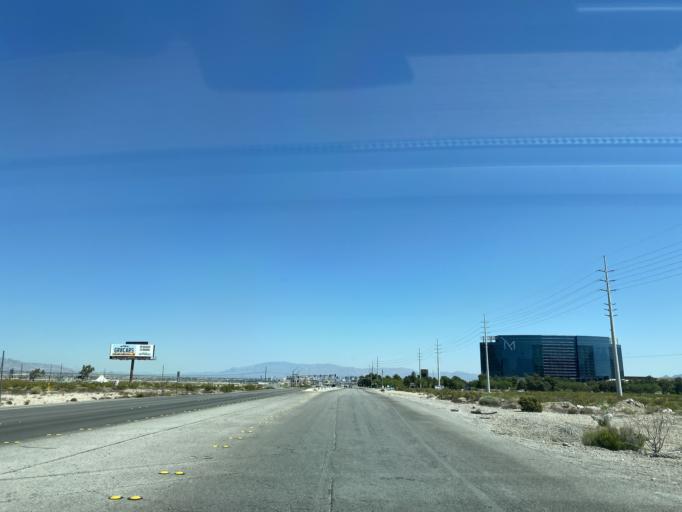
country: US
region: Nevada
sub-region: Clark County
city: Enterprise
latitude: 35.9593
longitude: -115.1729
